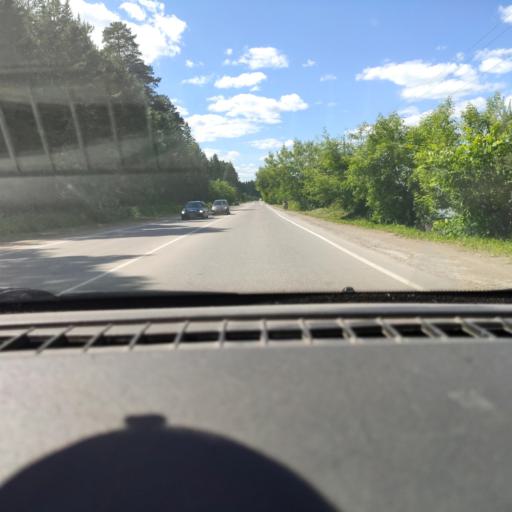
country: RU
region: Perm
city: Krasnokamsk
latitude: 58.0761
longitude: 55.6851
